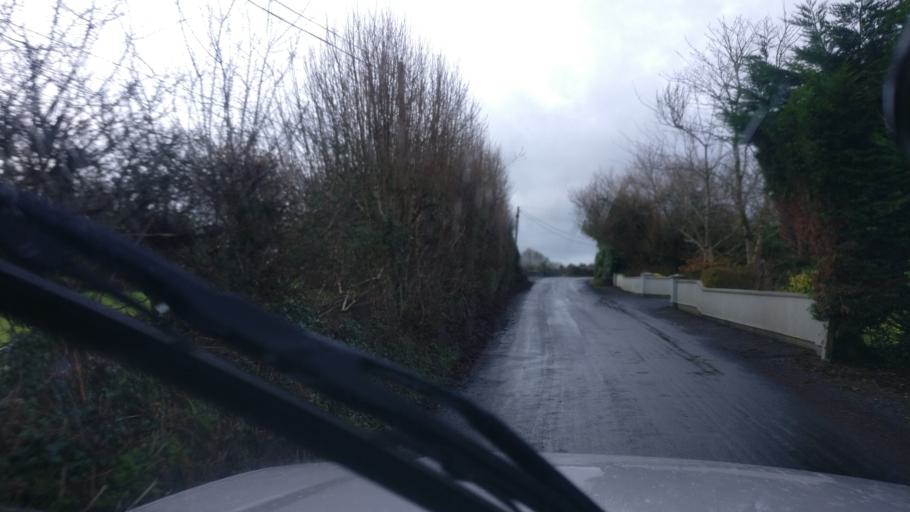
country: IE
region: Connaught
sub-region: County Galway
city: Athenry
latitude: 53.2683
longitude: -8.7761
